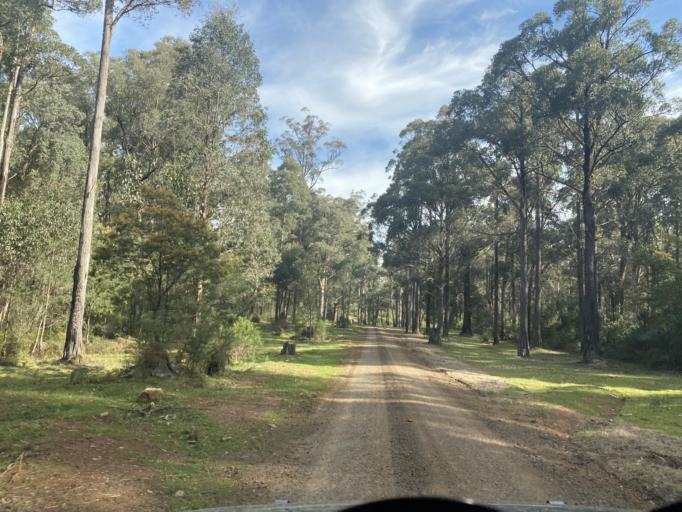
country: AU
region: Victoria
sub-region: Mansfield
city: Mansfield
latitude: -36.8455
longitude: 146.1815
